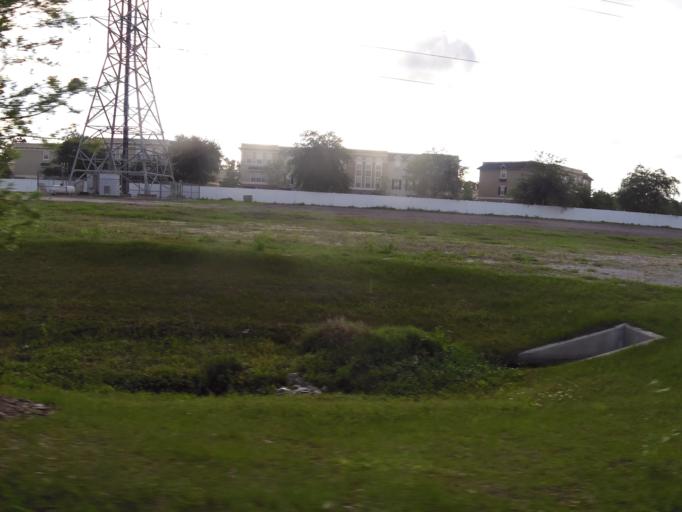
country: US
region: Florida
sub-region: Duval County
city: Jacksonville Beach
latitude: 30.2631
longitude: -81.5215
